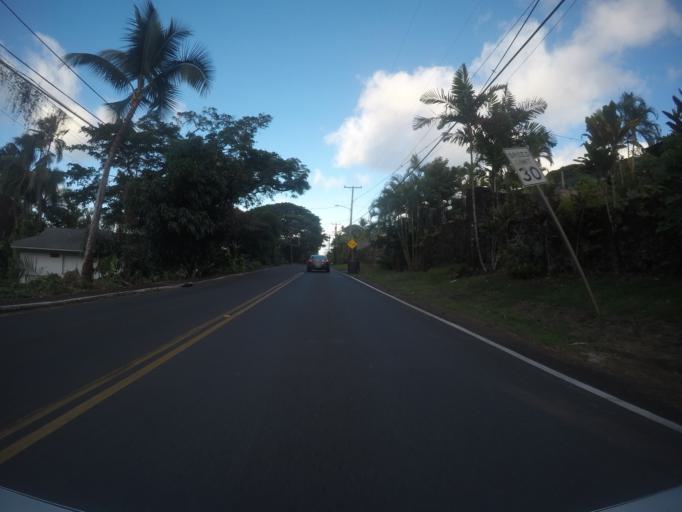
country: US
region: Hawaii
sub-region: Honolulu County
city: Kahalu'u
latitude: 21.4566
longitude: -157.8306
